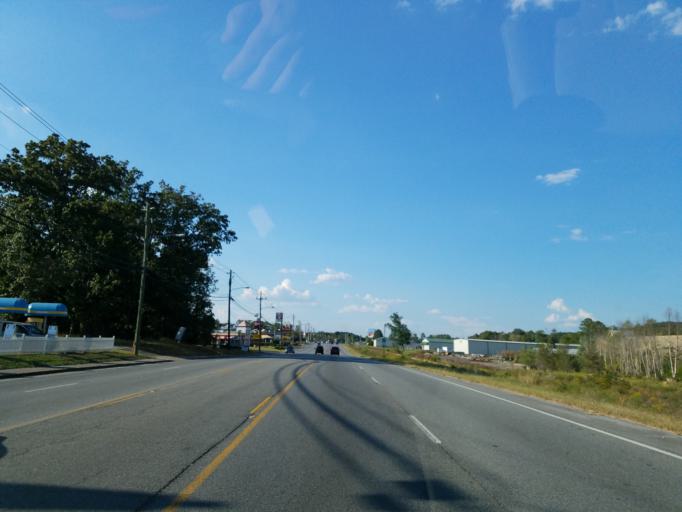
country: US
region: Georgia
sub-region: Murray County
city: Chatsworth
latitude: 34.7826
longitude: -84.7701
